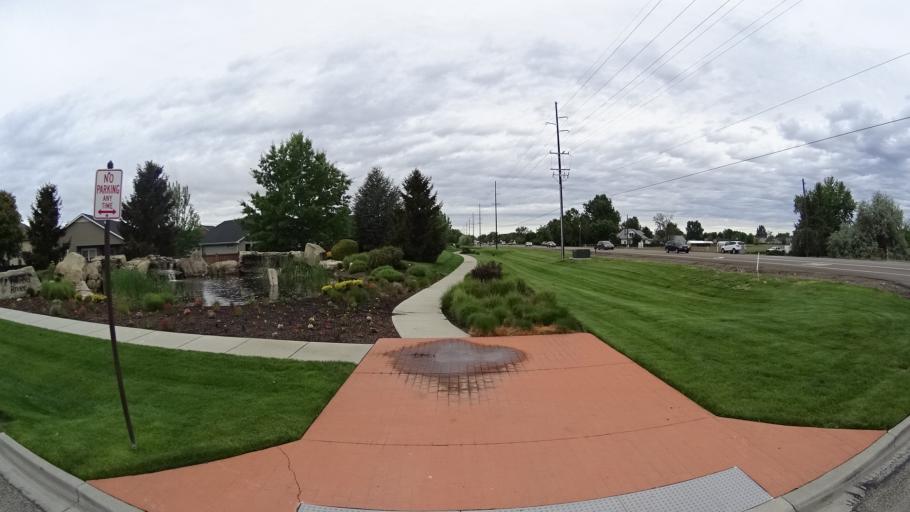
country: US
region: Idaho
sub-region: Ada County
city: Star
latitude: 43.6917
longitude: -116.4782
